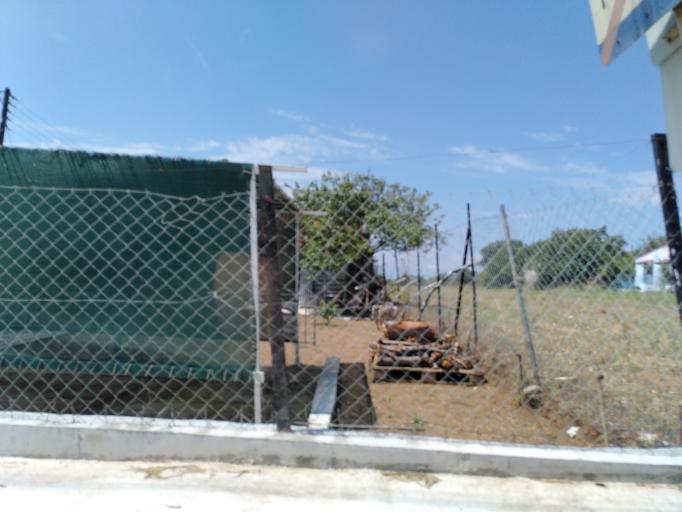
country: GR
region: Central Macedonia
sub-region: Nomos Thessalonikis
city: Nea Michaniona
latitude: 40.4433
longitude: 22.8690
